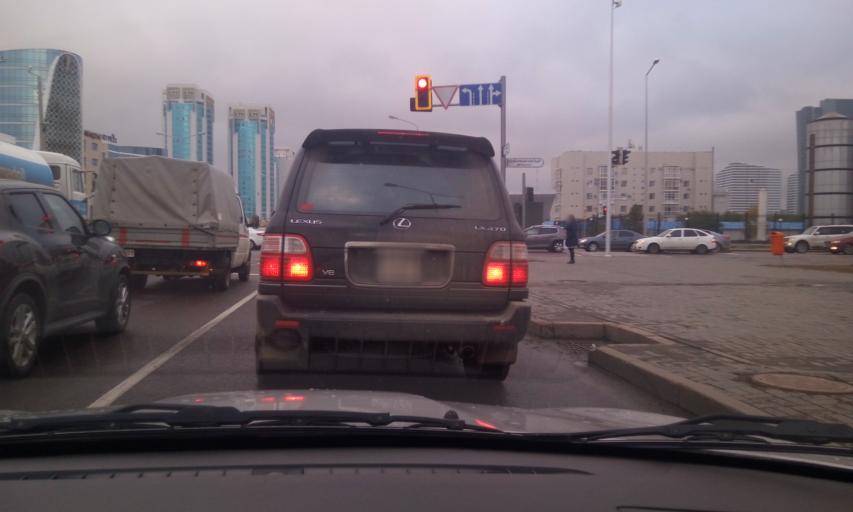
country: KZ
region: Astana Qalasy
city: Astana
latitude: 51.1365
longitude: 71.4151
